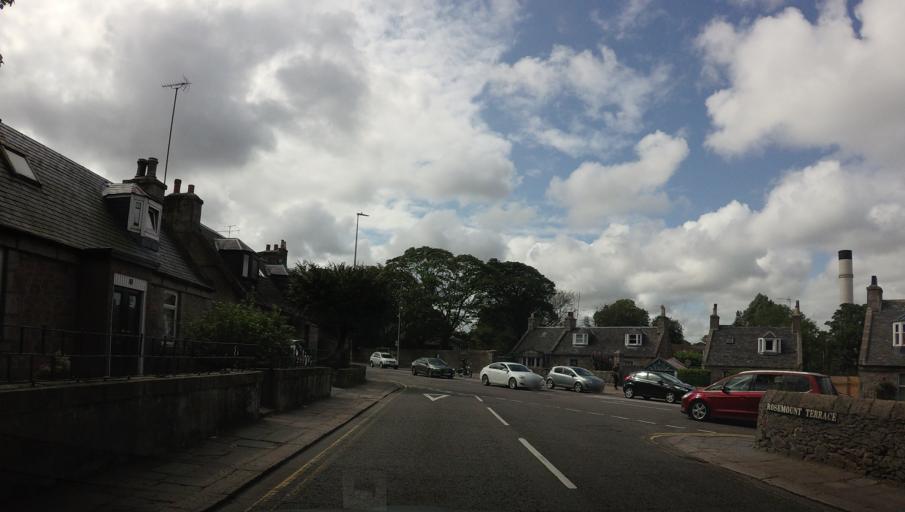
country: GB
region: Scotland
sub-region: Aberdeen City
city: Aberdeen
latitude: 57.1530
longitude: -2.1130
